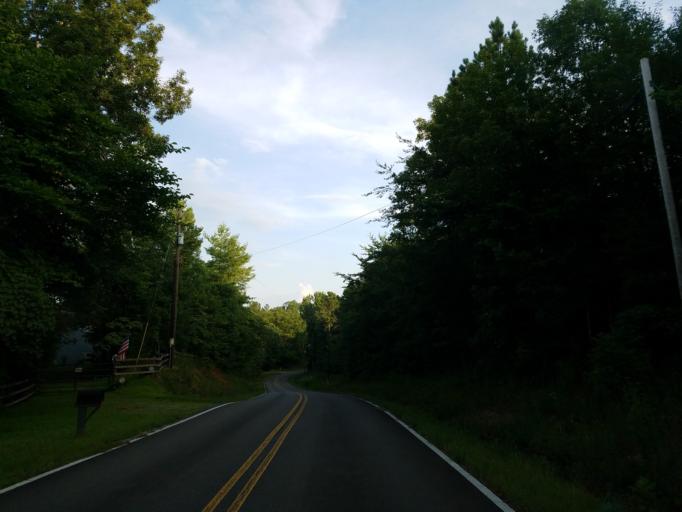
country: US
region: Georgia
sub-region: Pickens County
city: Jasper
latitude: 34.5000
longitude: -84.4203
